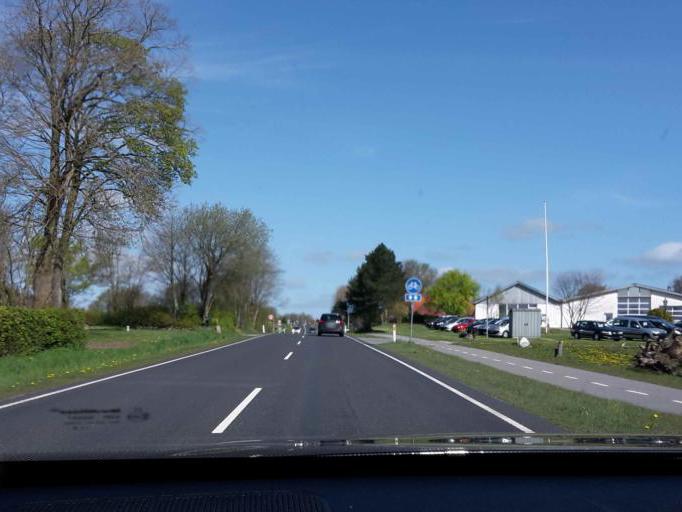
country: DK
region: South Denmark
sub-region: Vejen Kommune
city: Vejen
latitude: 55.5191
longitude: 9.1215
